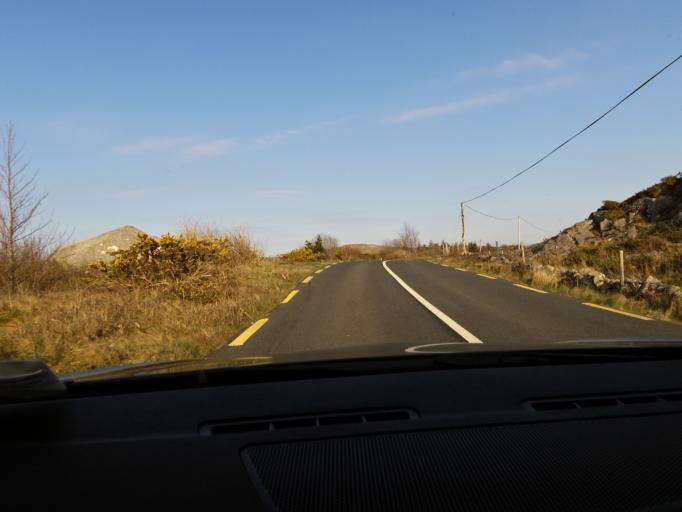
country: IE
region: Connaught
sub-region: County Galway
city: Oughterard
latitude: 53.3910
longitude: -9.6381
